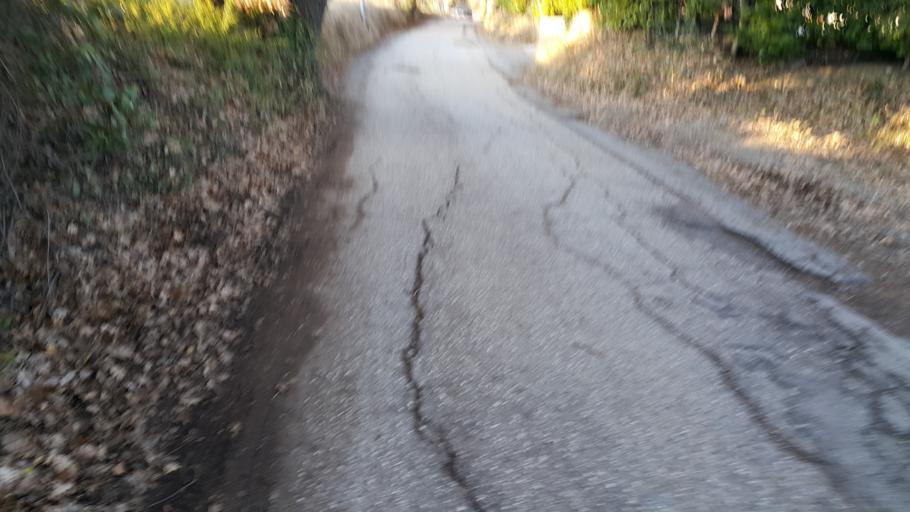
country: IT
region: Umbria
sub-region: Provincia di Perugia
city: Perugia
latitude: 43.0871
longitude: 12.3783
